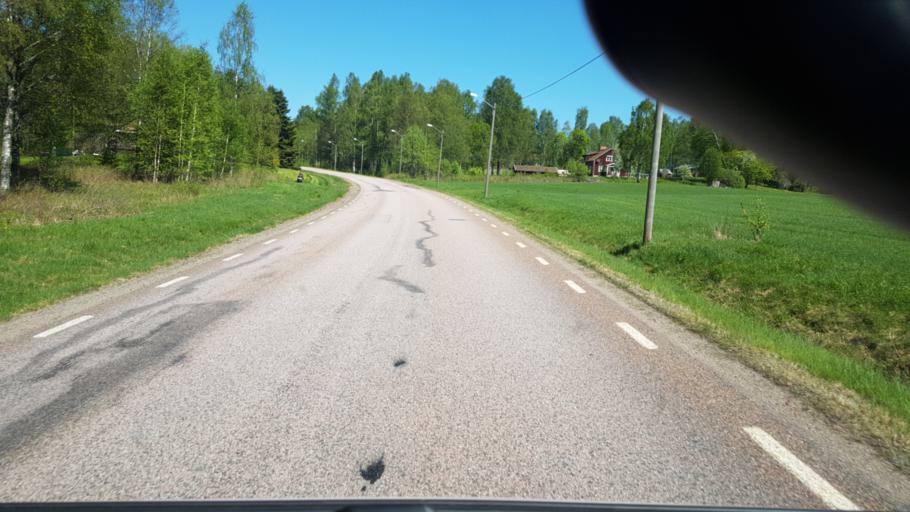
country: SE
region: Vaermland
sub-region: Arvika Kommun
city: Arvika
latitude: 59.8905
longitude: 12.6352
